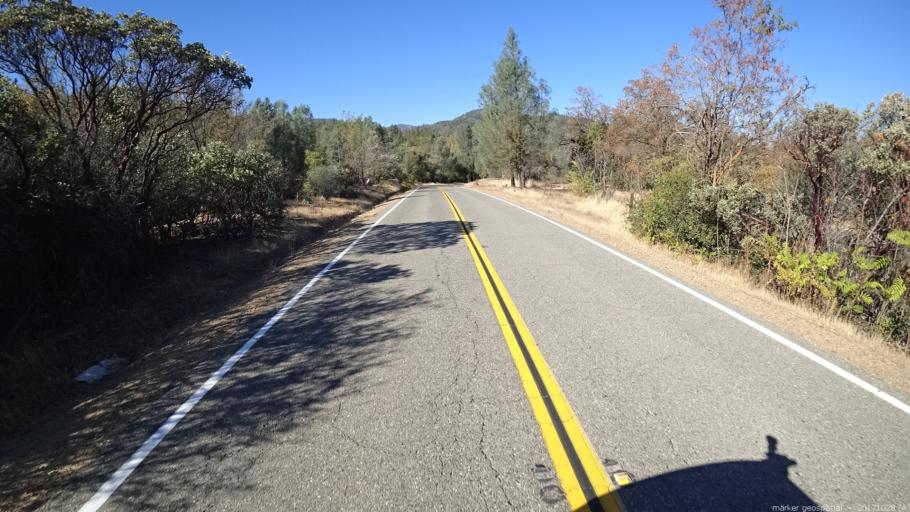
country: US
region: California
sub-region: Shasta County
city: Shasta
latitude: 40.6217
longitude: -122.4657
